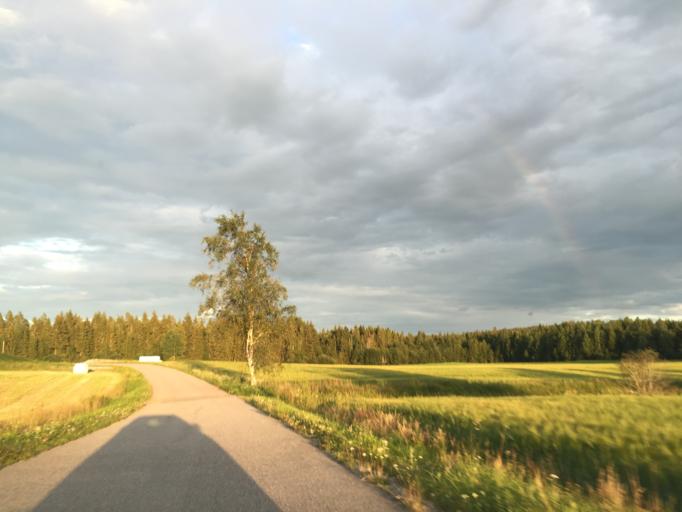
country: NO
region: Akershus
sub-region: Nes
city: Fjellfoten
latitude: 60.0907
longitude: 11.4873
